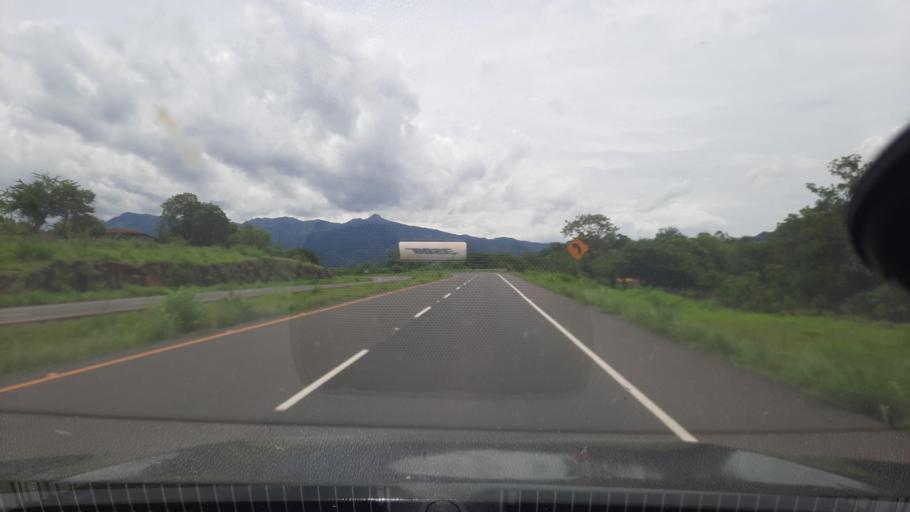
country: HN
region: Valle
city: Aramecina
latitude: 13.7579
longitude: -87.7121
